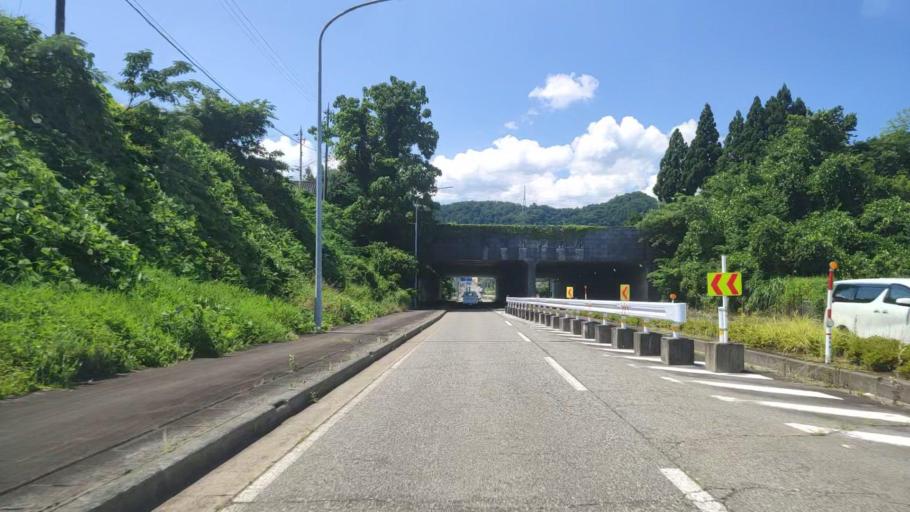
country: JP
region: Fukui
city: Katsuyama
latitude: 36.0287
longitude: 136.5186
